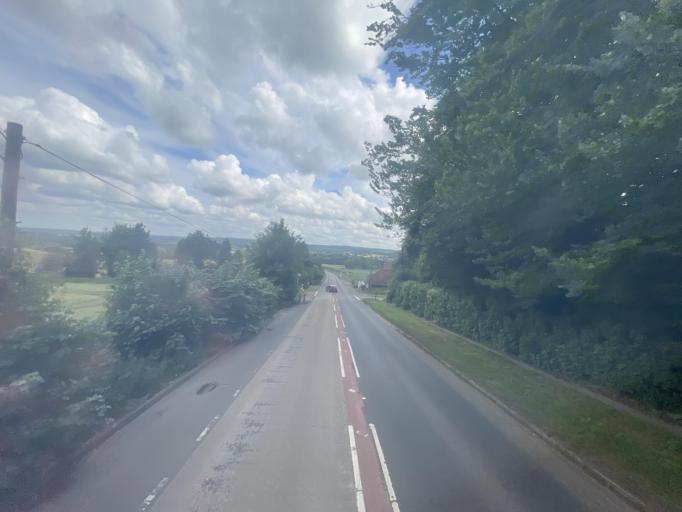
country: GB
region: England
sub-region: Kent
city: Westerham
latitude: 51.2837
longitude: 0.0650
